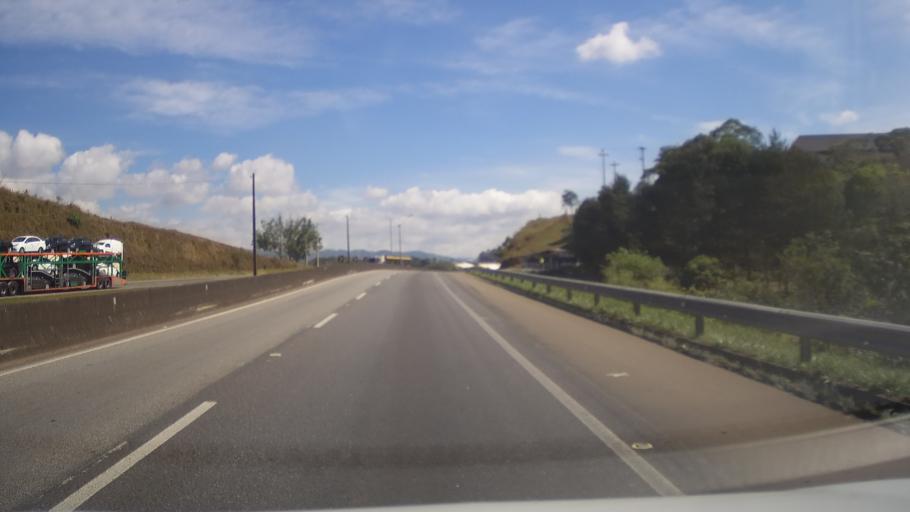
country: BR
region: Minas Gerais
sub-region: Cambui
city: Cambui
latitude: -22.5653
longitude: -46.0409
